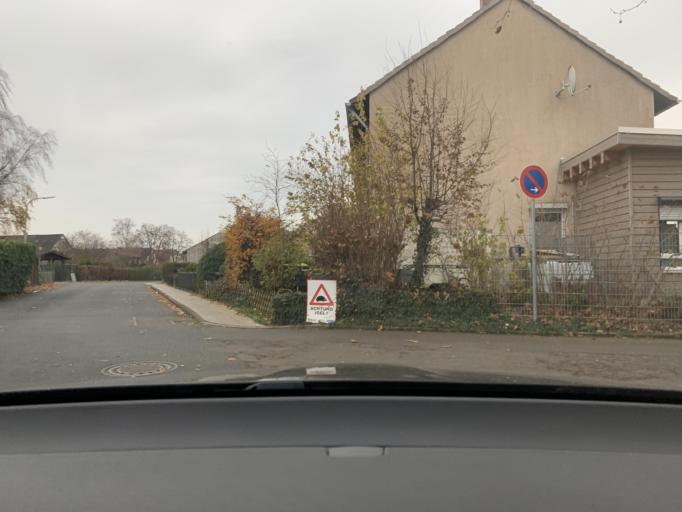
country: DE
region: Lower Saxony
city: Vordorf
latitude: 52.3192
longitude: 10.5102
